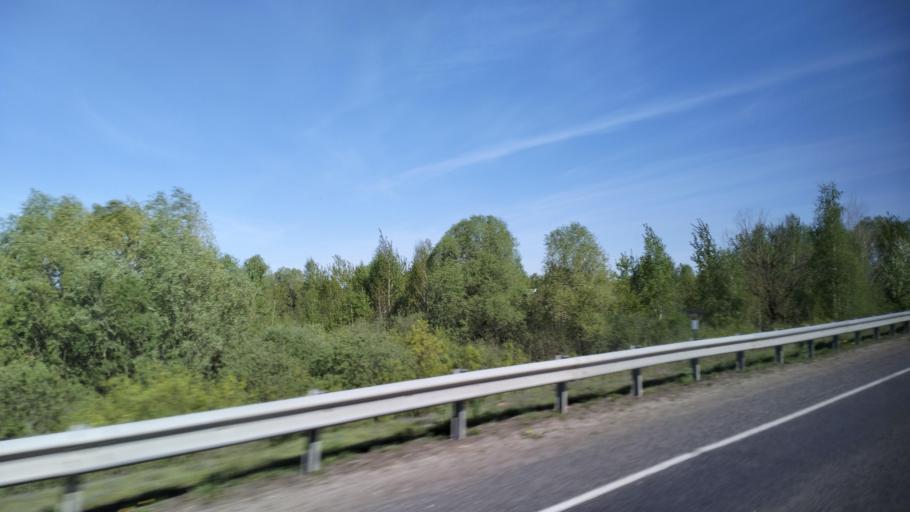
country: BY
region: Gomel
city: Turaw
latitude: 52.0949
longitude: 27.8297
